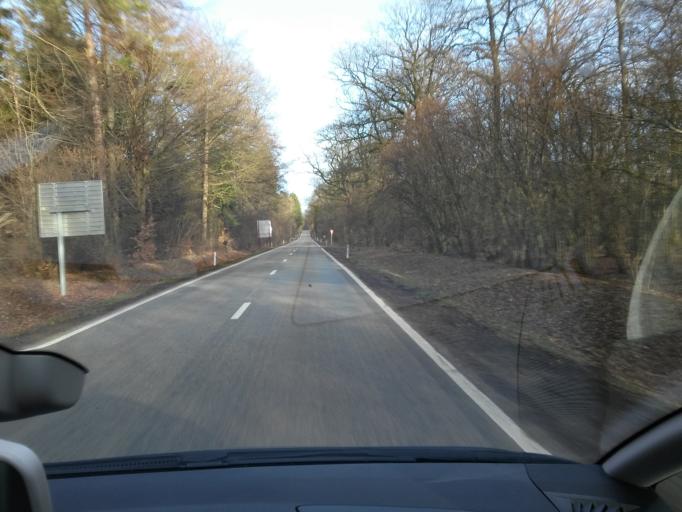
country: BE
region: Wallonia
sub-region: Province du Luxembourg
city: Daverdisse
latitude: 50.0139
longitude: 5.1825
